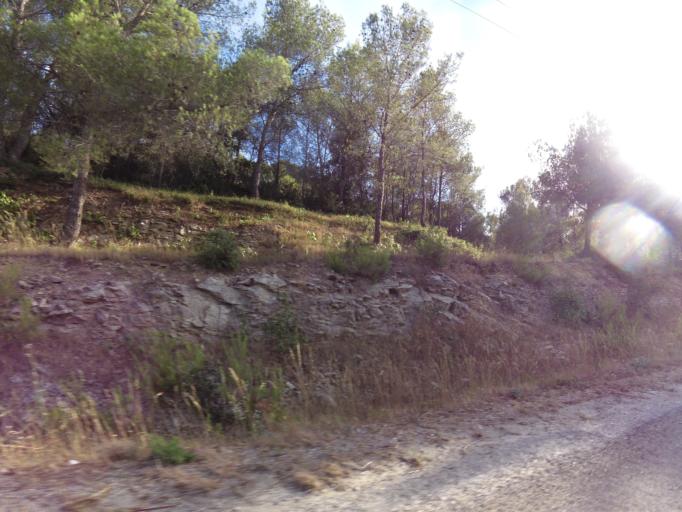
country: FR
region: Languedoc-Roussillon
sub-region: Departement du Gard
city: Calvisson
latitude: 43.7873
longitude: 4.1750
